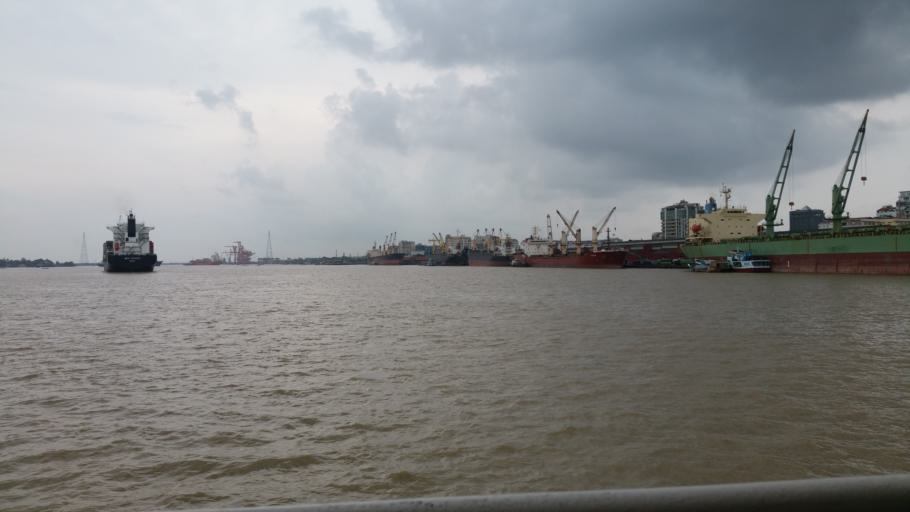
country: MM
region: Yangon
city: Yangon
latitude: 16.7667
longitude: 96.1593
